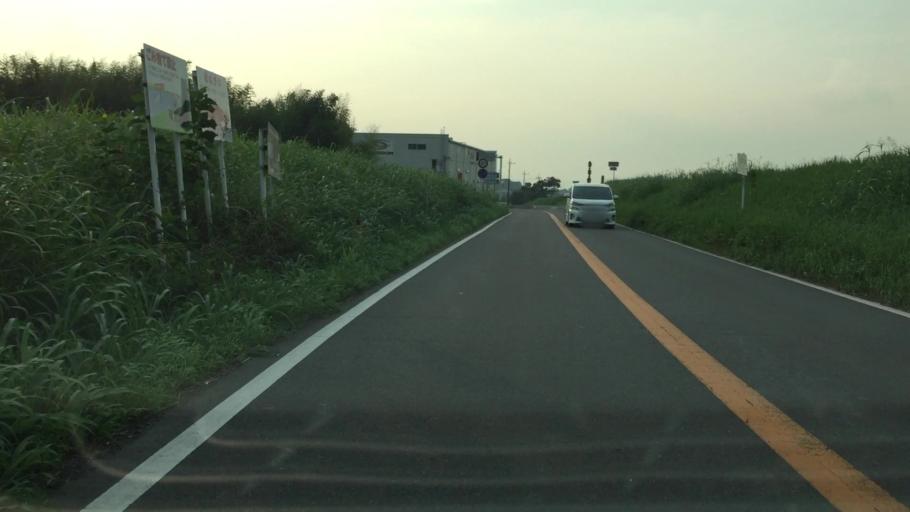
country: JP
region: Tochigi
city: Fujioka
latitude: 36.2612
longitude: 139.6371
